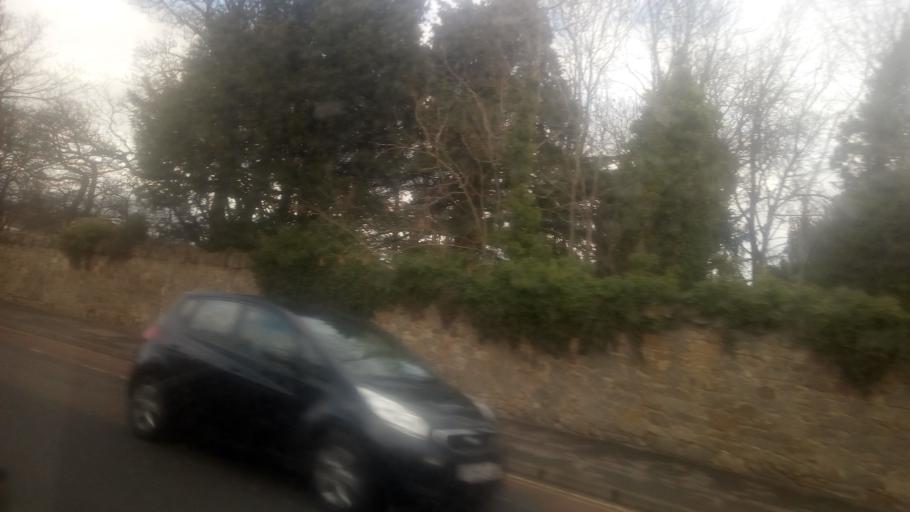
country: GB
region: Scotland
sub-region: Midlothian
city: Loanhead
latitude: 55.9158
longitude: -3.1301
